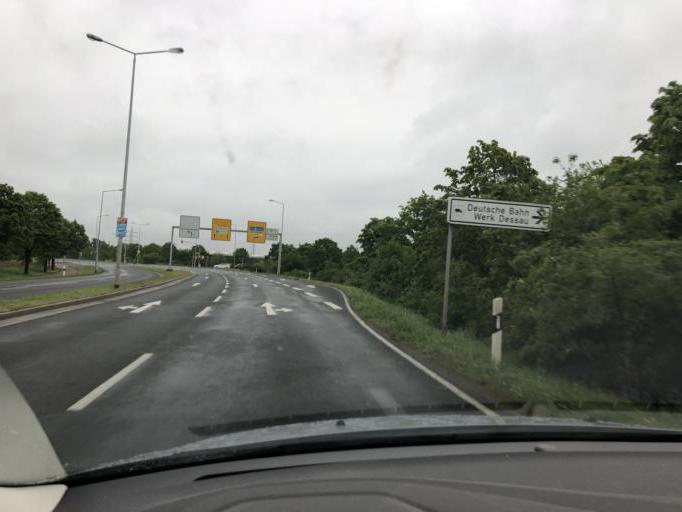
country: DE
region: Saxony-Anhalt
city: Dessau
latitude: 51.8088
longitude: 12.2223
